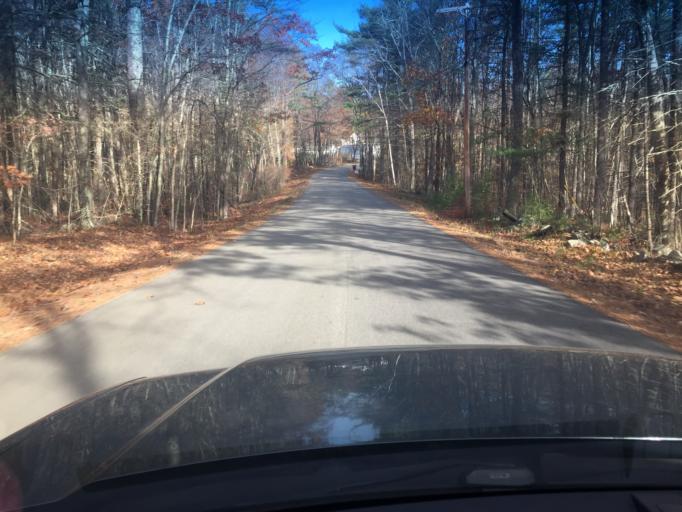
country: US
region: Maine
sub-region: York County
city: Eliot
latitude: 43.1938
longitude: -70.7483
